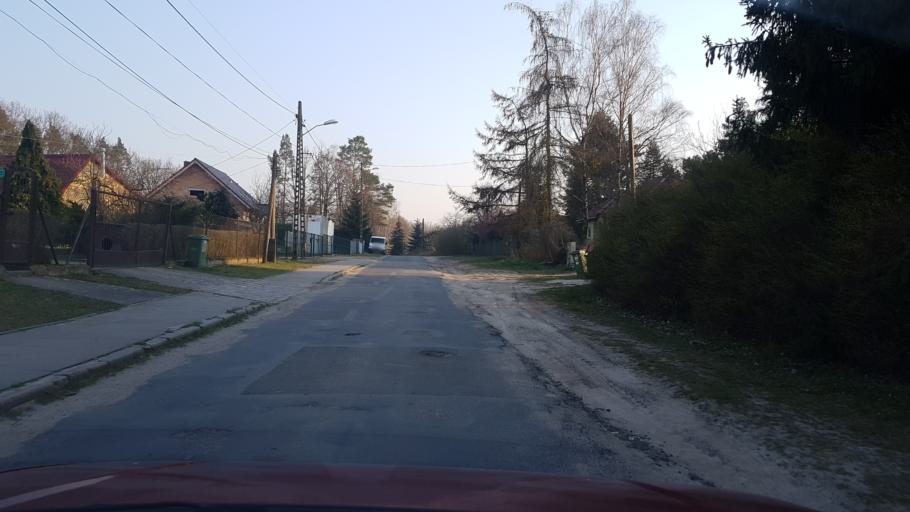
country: PL
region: West Pomeranian Voivodeship
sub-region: Powiat gryfinski
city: Stare Czarnowo
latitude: 53.3355
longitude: 14.7499
